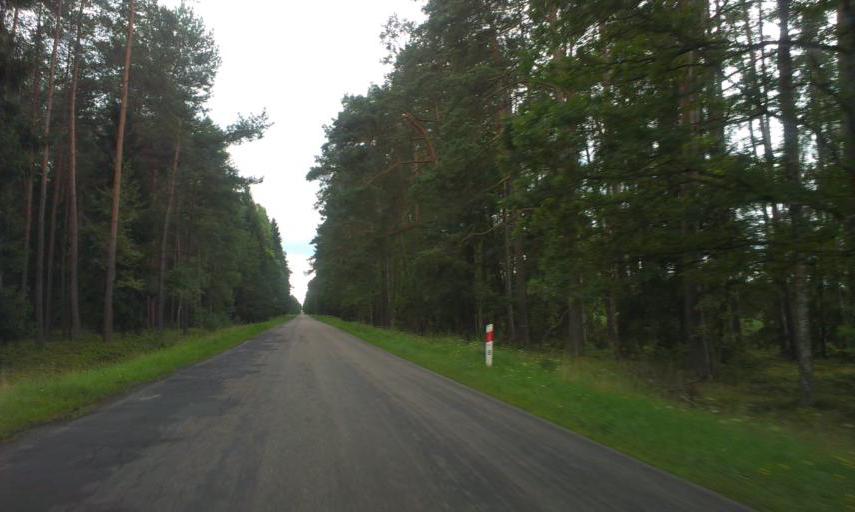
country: PL
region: West Pomeranian Voivodeship
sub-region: Powiat bialogardzki
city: Tychowo
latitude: 53.9569
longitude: 16.2252
